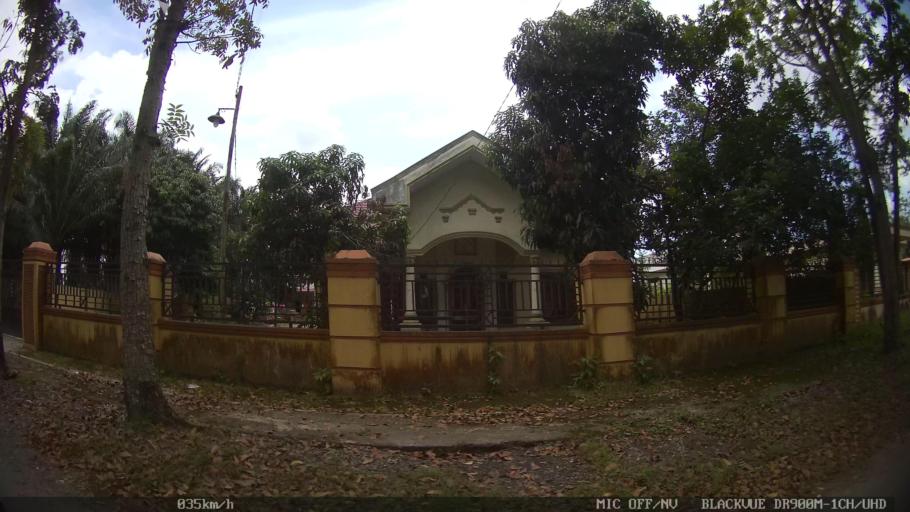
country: ID
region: North Sumatra
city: Binjai
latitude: 3.6208
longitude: 98.5107
